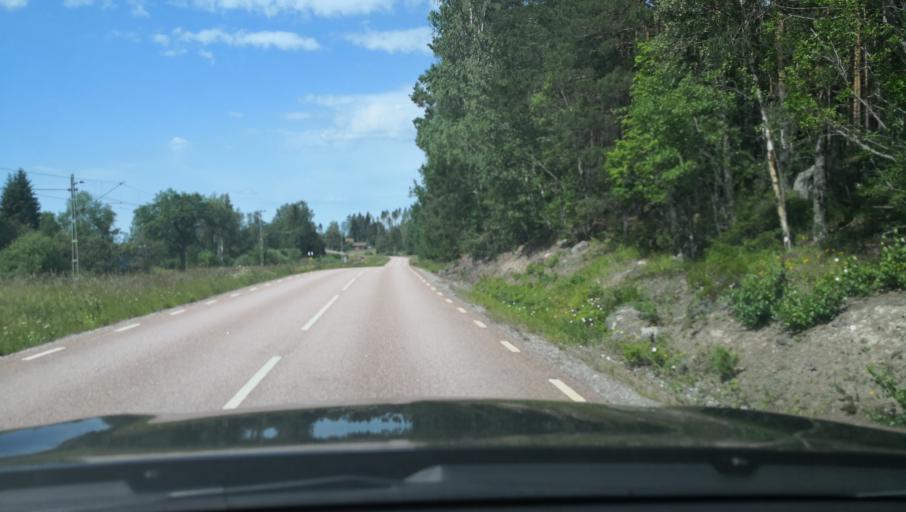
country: SE
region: Vaestmanland
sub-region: Surahammars Kommun
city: Ramnas
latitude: 59.8533
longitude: 16.0961
